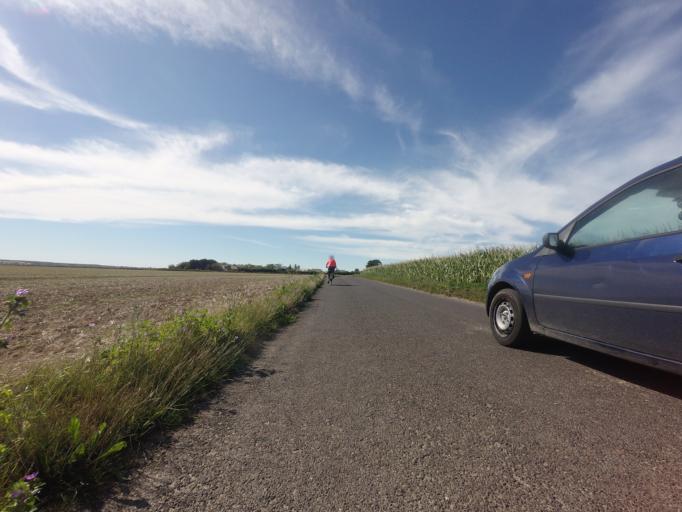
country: GB
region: England
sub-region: Kent
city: Birchington-on-Sea
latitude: 51.3483
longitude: 1.2586
